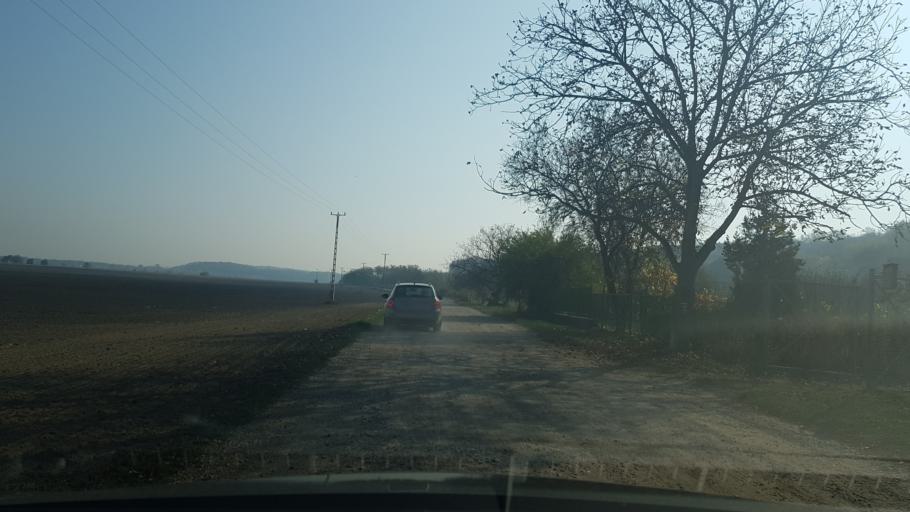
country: HU
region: Fejer
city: Adony
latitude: 47.0836
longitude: 18.8502
